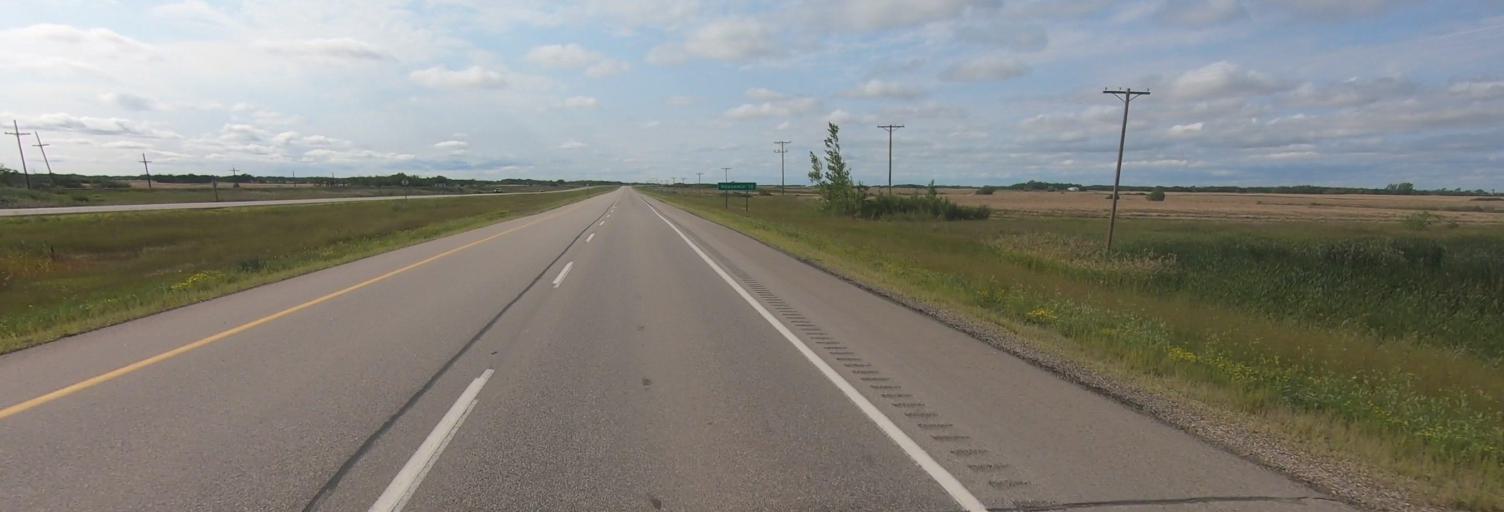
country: CA
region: Saskatchewan
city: Moosomin
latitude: 50.0789
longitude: -101.5172
